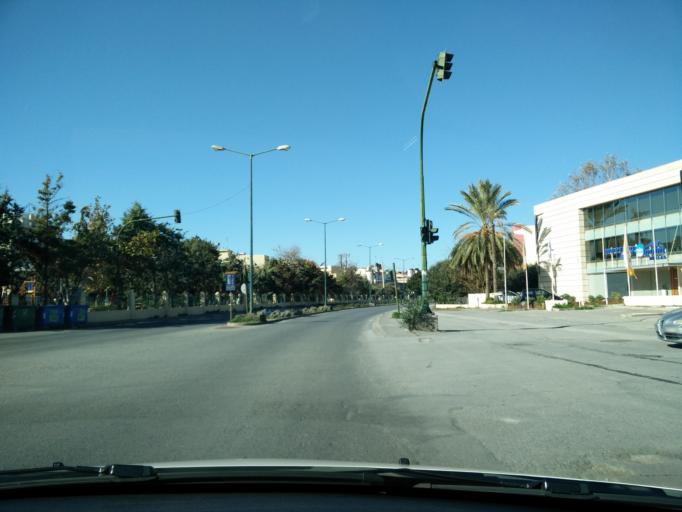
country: GR
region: Crete
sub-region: Nomos Irakleiou
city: Nea Alikarnassos
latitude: 35.3366
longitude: 25.1554
